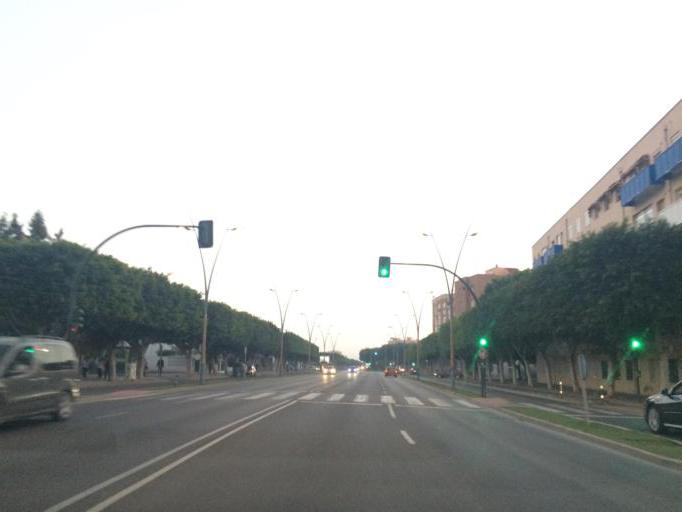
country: ES
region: Andalusia
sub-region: Provincia de Almeria
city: Almeria
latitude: 36.8337
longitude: -2.4466
